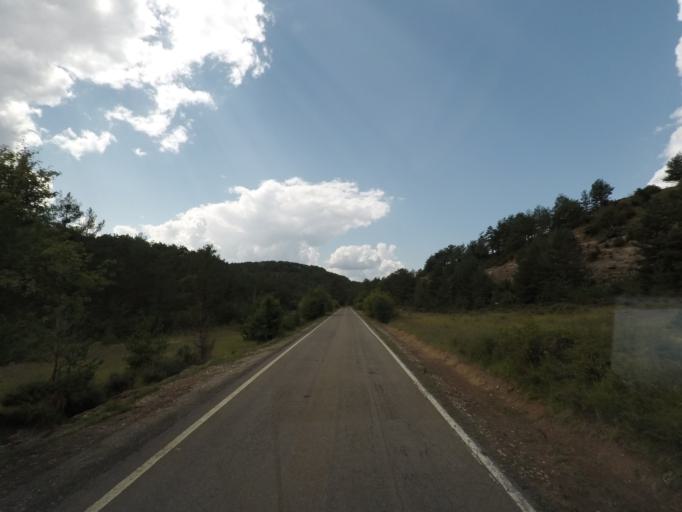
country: ES
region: Aragon
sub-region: Provincia de Huesca
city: Fiscal
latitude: 42.4059
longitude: -0.1769
